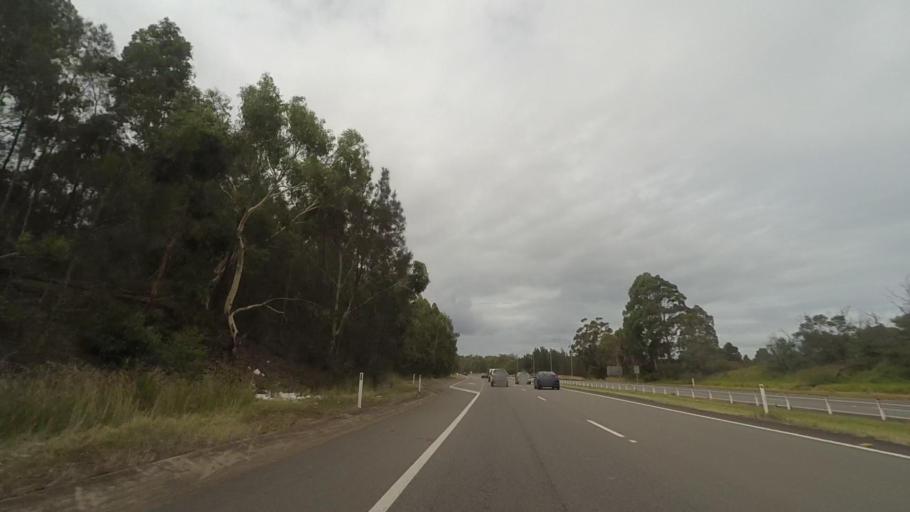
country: AU
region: New South Wales
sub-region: Port Stephens Shire
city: Raymond Terrace
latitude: -32.7434
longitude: 151.7743
